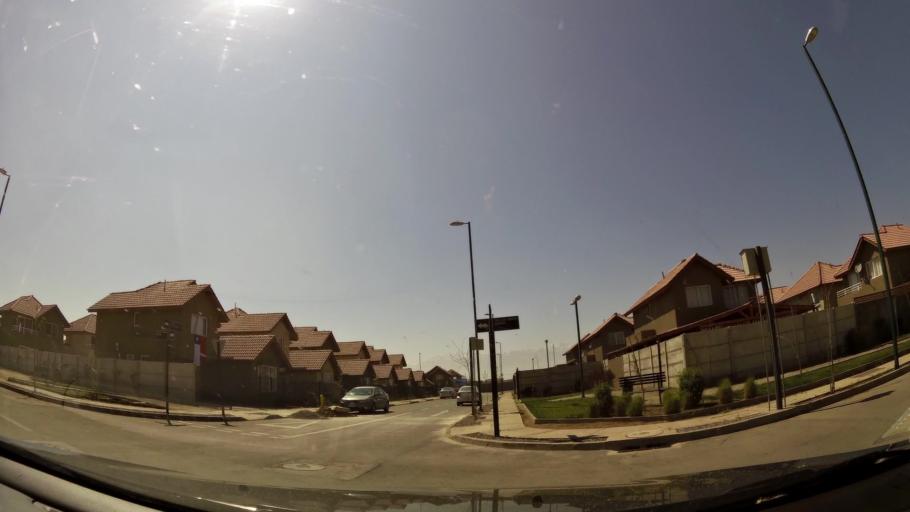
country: CL
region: Santiago Metropolitan
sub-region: Provincia de Chacabuco
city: Chicureo Abajo
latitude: -33.3223
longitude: -70.7560
